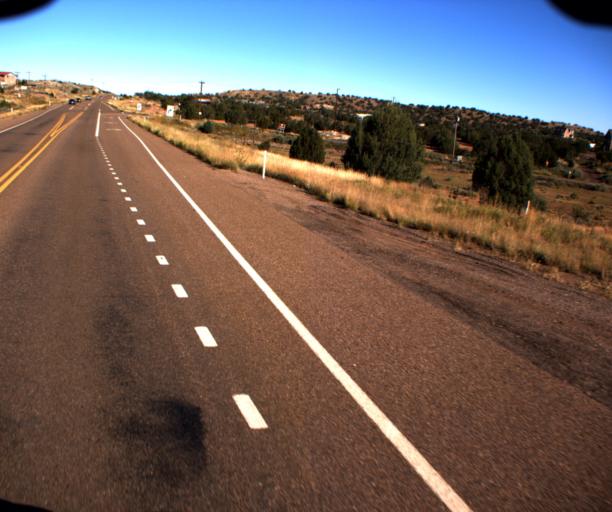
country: US
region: Arizona
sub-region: Navajo County
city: Taylor
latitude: 34.4051
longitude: -110.0759
